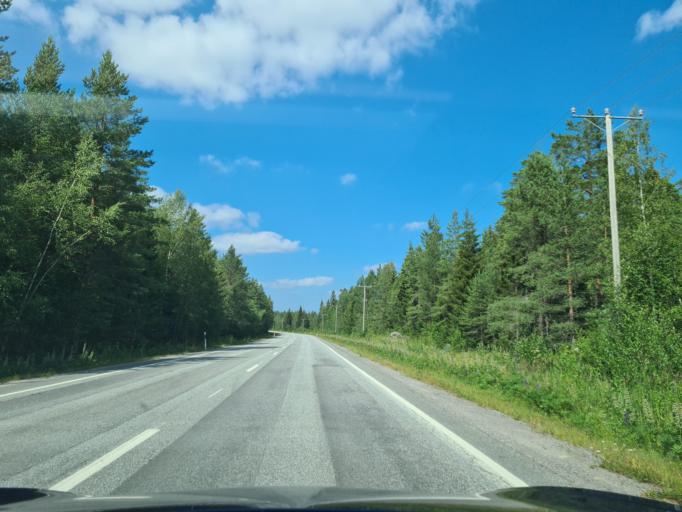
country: FI
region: Ostrobothnia
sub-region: Vaasa
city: Vaasa
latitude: 63.1763
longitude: 21.5772
